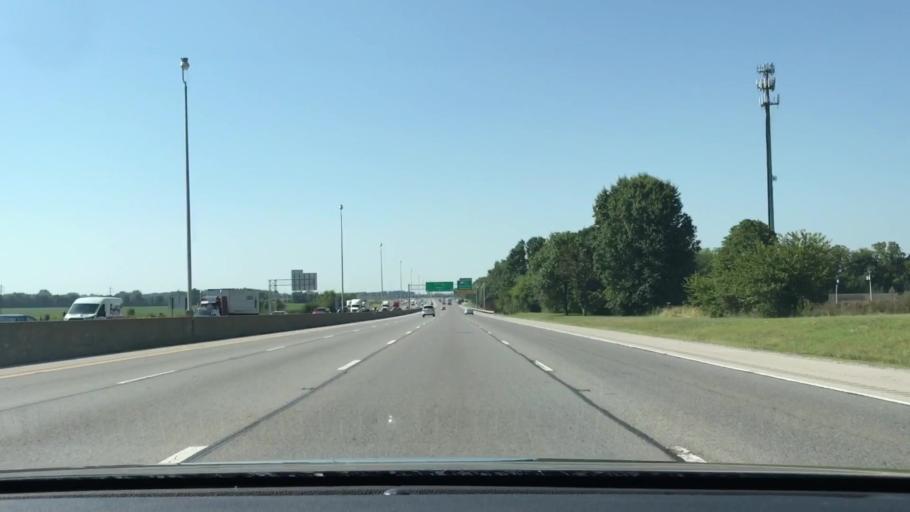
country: US
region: Kentucky
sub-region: Warren County
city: Plano
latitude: 36.9224
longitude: -86.4257
